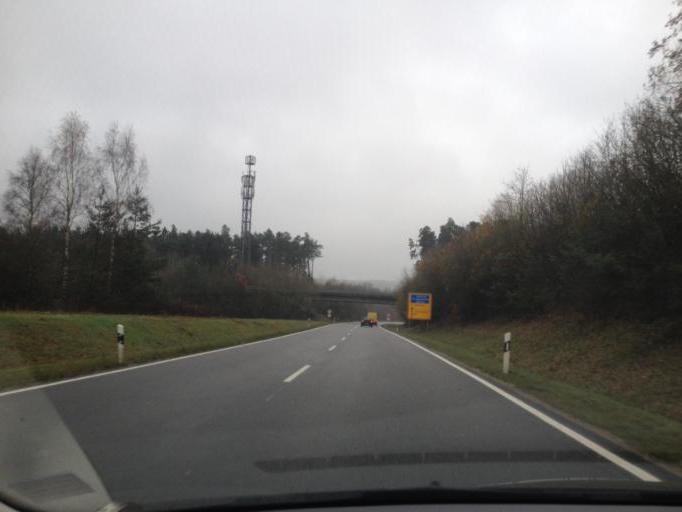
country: DE
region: Bavaria
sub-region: Regierungsbezirk Mittelfranken
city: Heroldsberg
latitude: 49.5283
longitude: 11.1683
